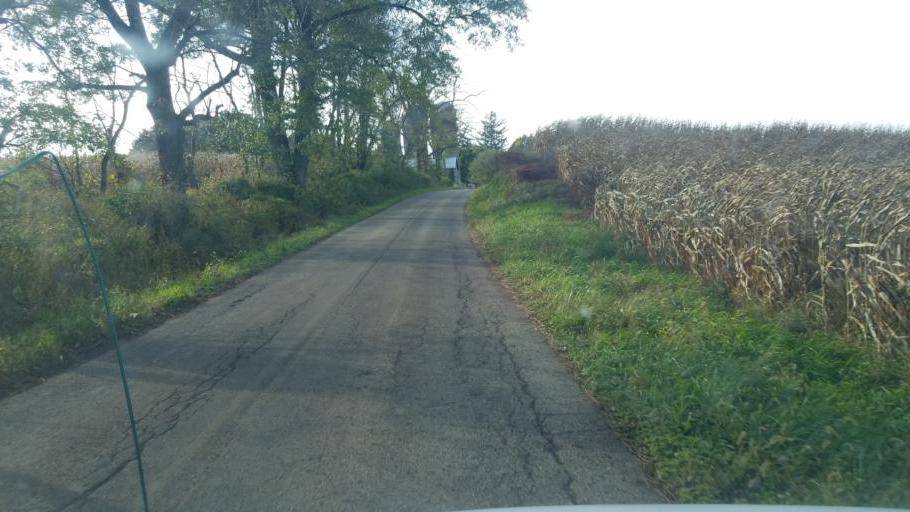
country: US
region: Ohio
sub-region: Wayne County
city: Shreve
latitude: 40.6482
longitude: -82.0561
